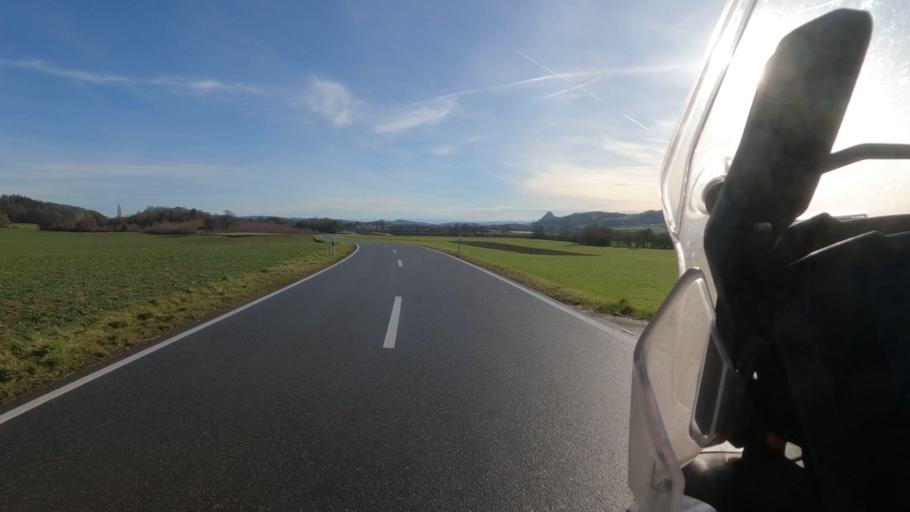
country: DE
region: Baden-Wuerttemberg
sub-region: Freiburg Region
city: Neuhausen
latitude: 47.8330
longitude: 8.7811
